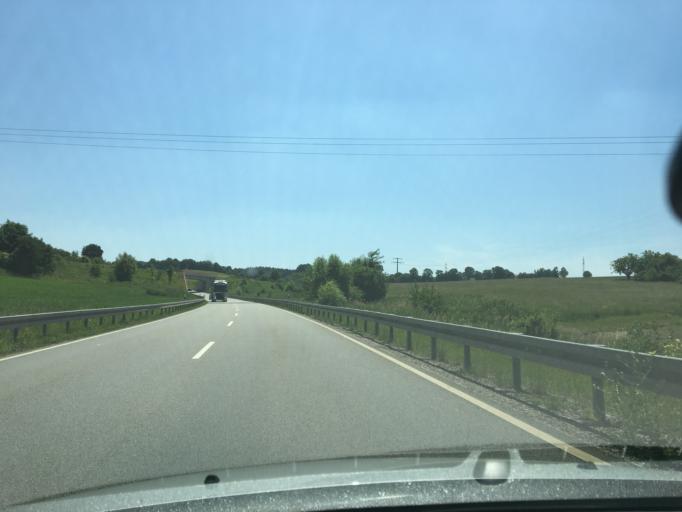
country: DE
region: Bavaria
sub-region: Upper Bavaria
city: Neumarkt-Sankt Veit
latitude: 48.3498
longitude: 12.4915
